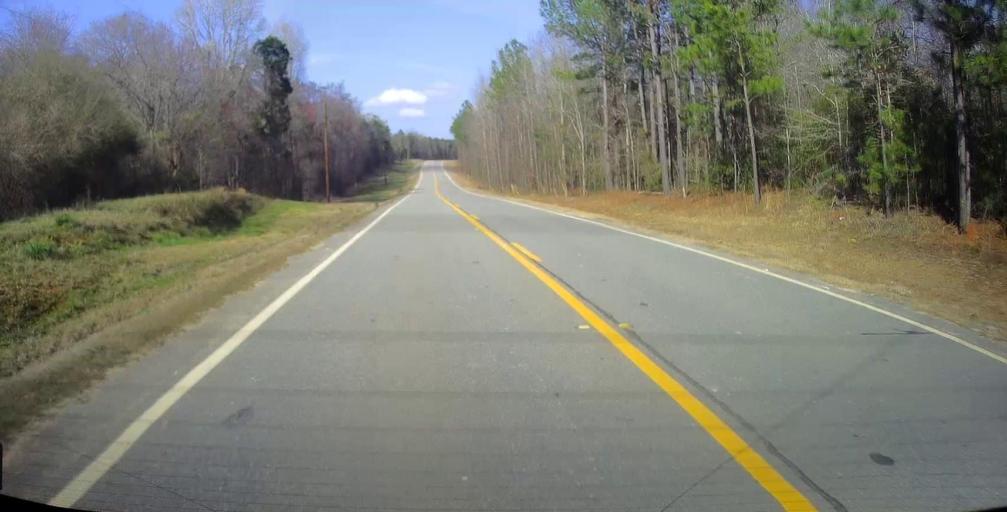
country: US
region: Georgia
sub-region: Wilkinson County
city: Gordon
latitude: 32.7933
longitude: -83.3315
